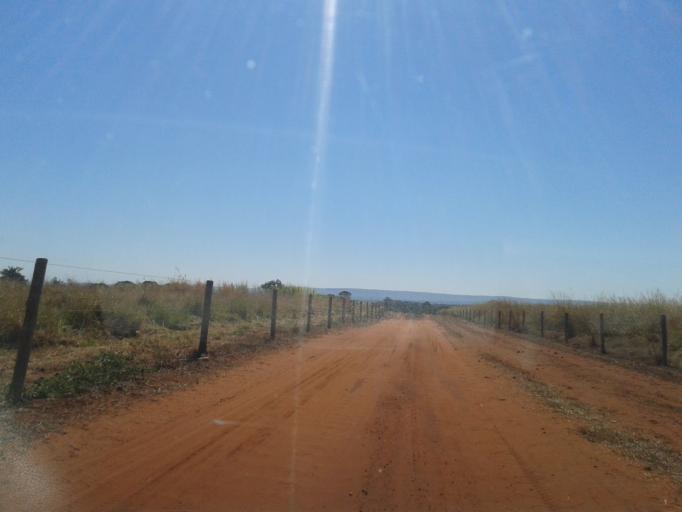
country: BR
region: Minas Gerais
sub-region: Santa Vitoria
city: Santa Vitoria
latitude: -19.1442
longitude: -50.2025
